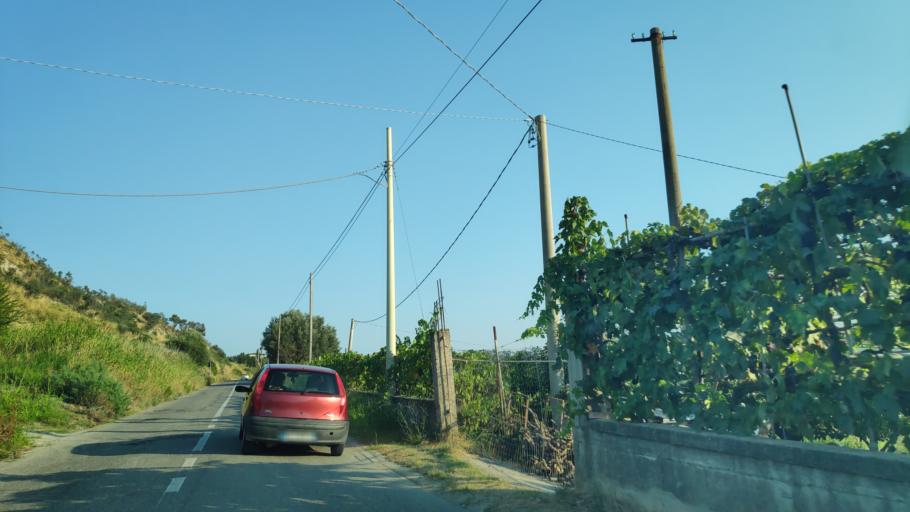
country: IT
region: Calabria
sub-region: Provincia di Reggio Calabria
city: Caulonia Marina
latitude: 38.3745
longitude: 16.4432
